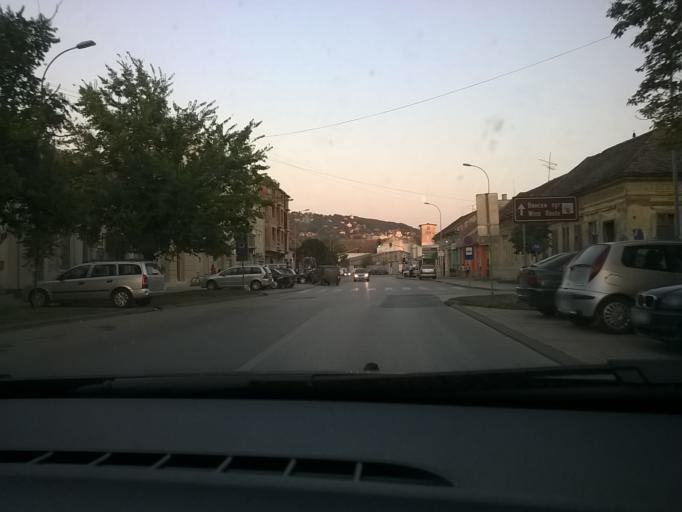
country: RS
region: Autonomna Pokrajina Vojvodina
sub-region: Juznobanatski Okrug
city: Vrsac
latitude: 45.1221
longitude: 21.3010
